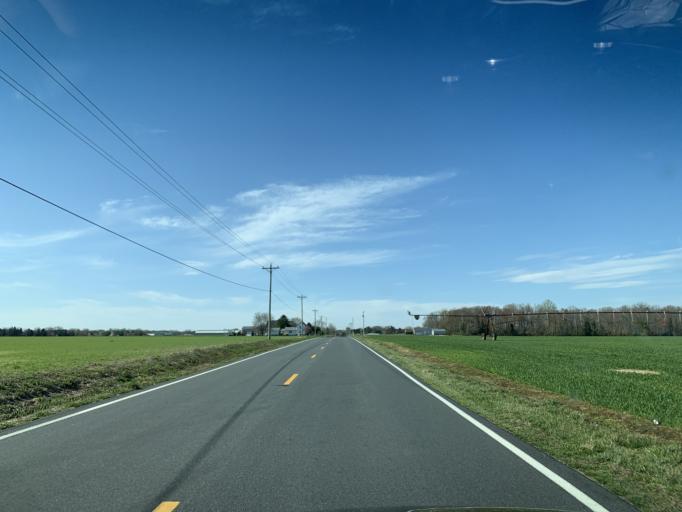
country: US
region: Delaware
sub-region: Kent County
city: Riverview
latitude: 39.0209
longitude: -75.5385
